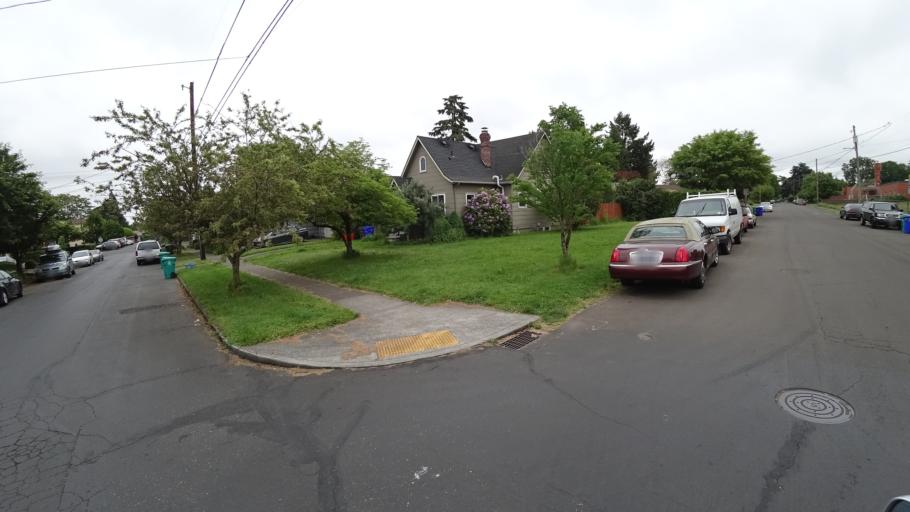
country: US
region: Oregon
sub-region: Multnomah County
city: Portland
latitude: 45.5602
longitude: -122.6214
